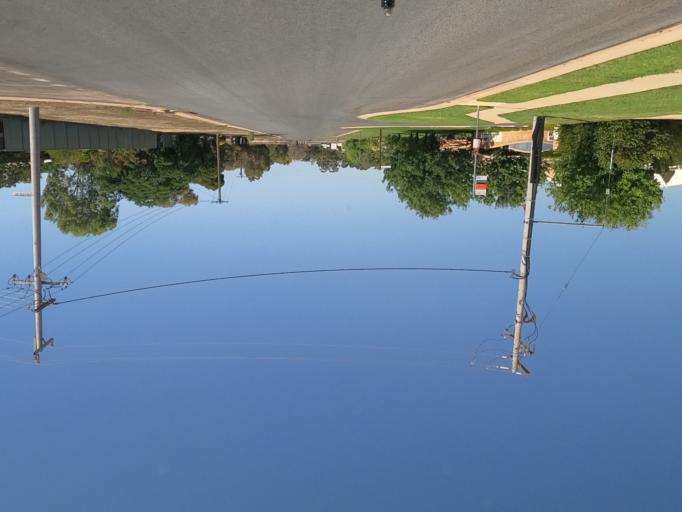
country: AU
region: New South Wales
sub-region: Corowa Shire
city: Mulwala
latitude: -35.9857
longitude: 146.0034
